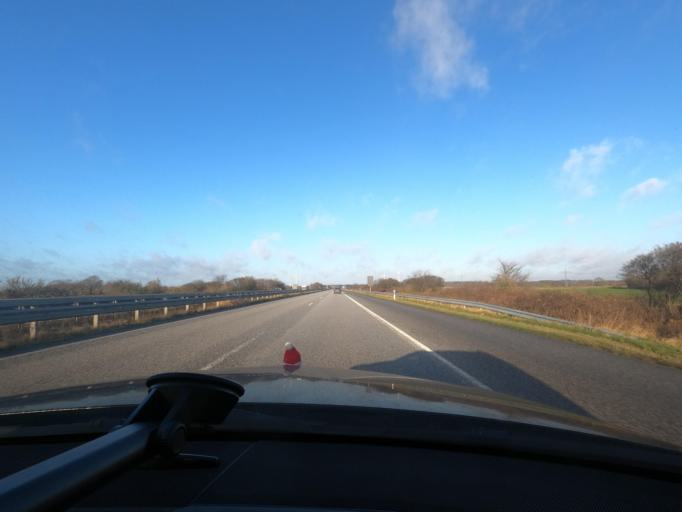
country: DE
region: Schleswig-Holstein
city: Bollingstedt
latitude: 54.6236
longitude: 9.4418
